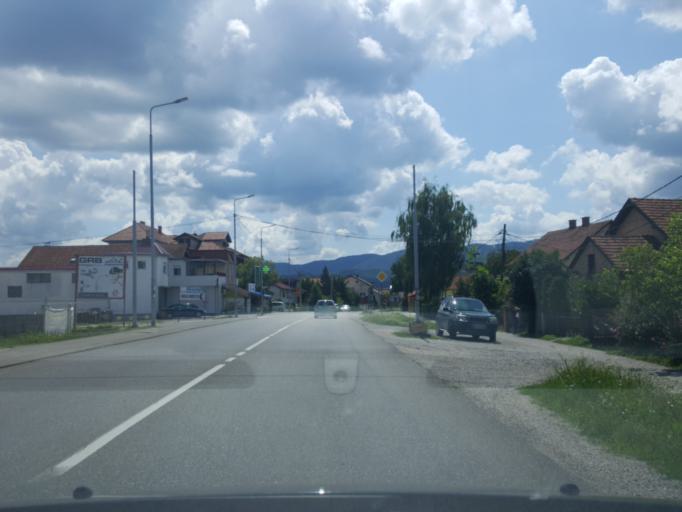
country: RS
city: Lipnicki Sor
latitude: 44.5443
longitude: 19.2309
